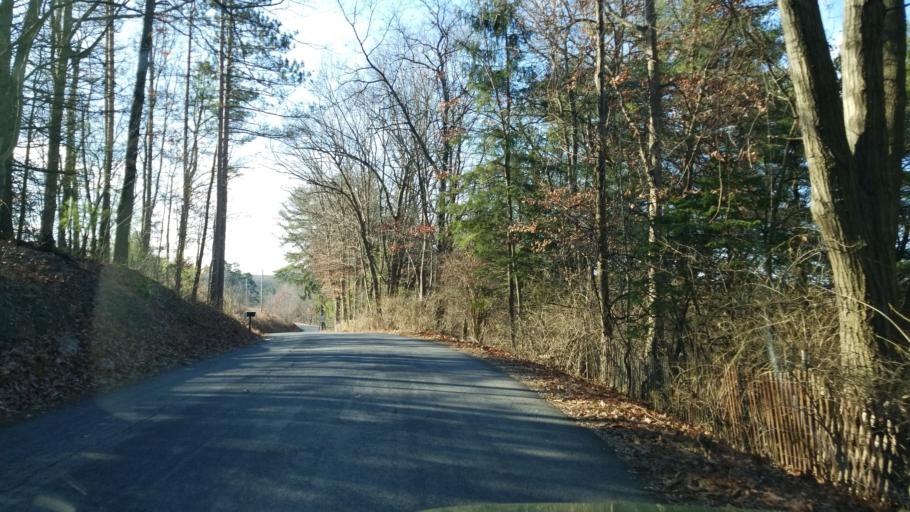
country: US
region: Pennsylvania
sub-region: Clearfield County
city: Clearfield
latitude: 41.0070
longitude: -78.4187
